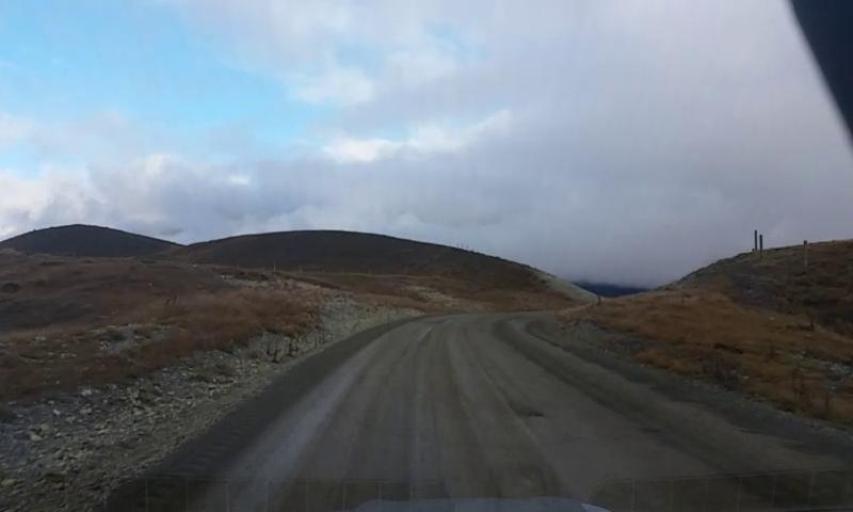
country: NZ
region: Canterbury
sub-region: Ashburton District
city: Methven
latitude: -43.6156
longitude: 171.1355
